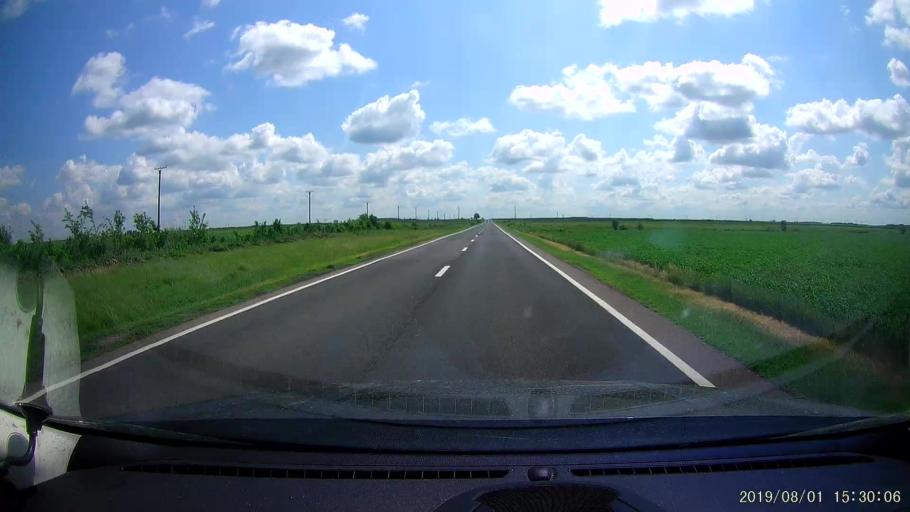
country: RO
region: Braila
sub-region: Comuna Viziru
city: Viziru
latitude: 44.9693
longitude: 27.6839
